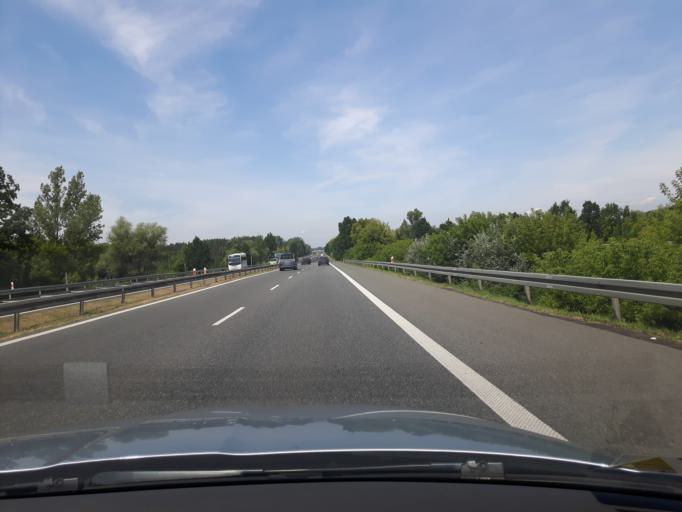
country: PL
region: Masovian Voivodeship
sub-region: Powiat nowodworski
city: Nowy Dwor Mazowiecki
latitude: 52.3963
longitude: 20.7173
